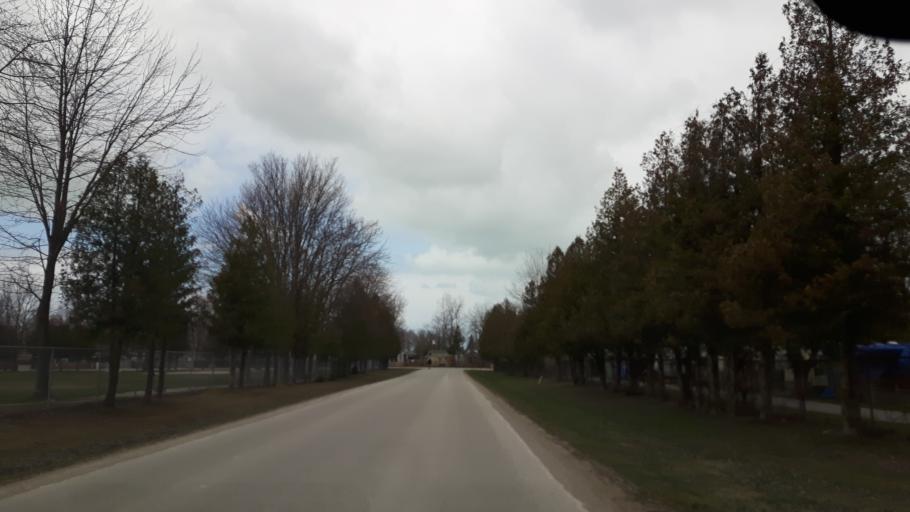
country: CA
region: Ontario
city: Bluewater
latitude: 43.5492
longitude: -81.6989
